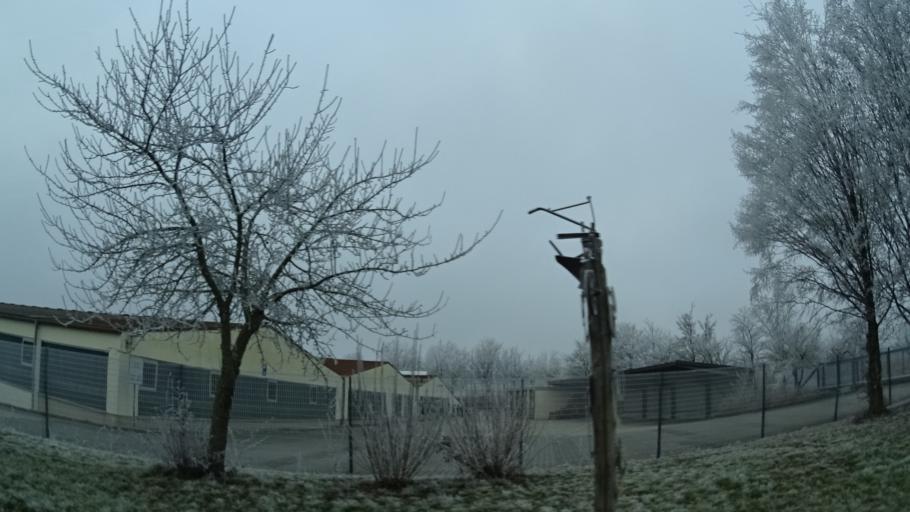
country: DE
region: Baden-Wuerttemberg
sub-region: Regierungsbezirk Stuttgart
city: Boxberg
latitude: 49.4569
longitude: 9.6079
